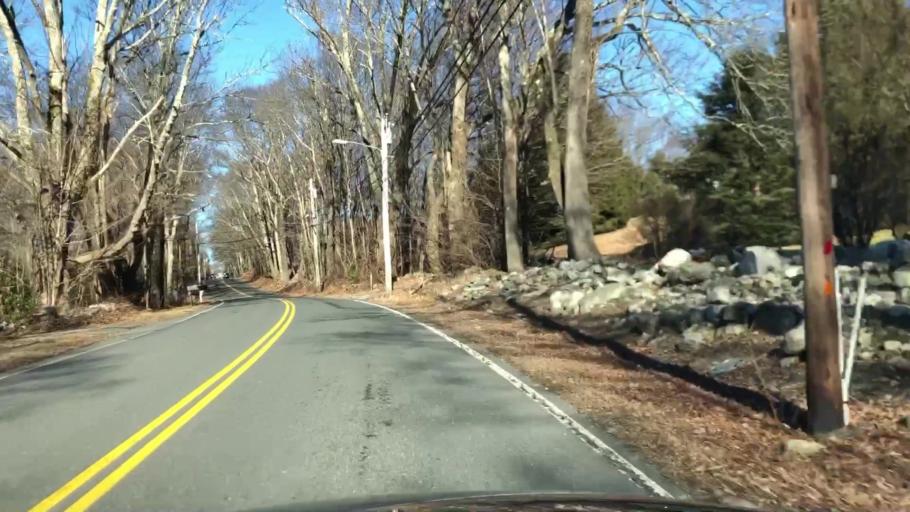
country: US
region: Massachusetts
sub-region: Worcester County
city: Charlton
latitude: 42.1129
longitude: -71.9703
